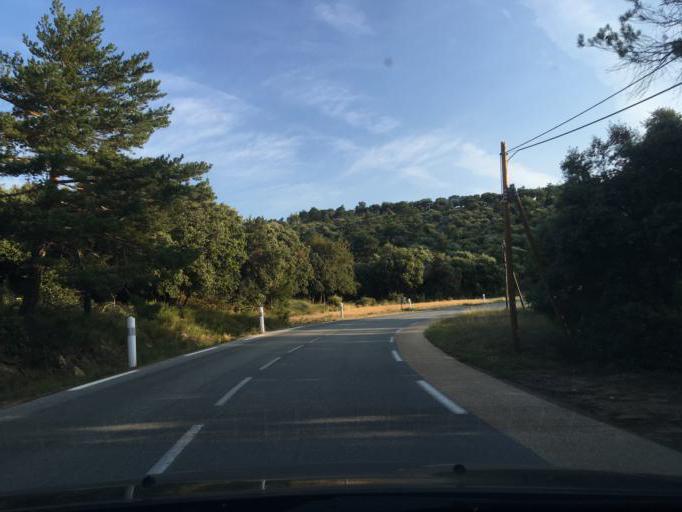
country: FR
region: Provence-Alpes-Cote d'Azur
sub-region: Departement du Var
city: Aups
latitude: 43.6596
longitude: 6.2225
